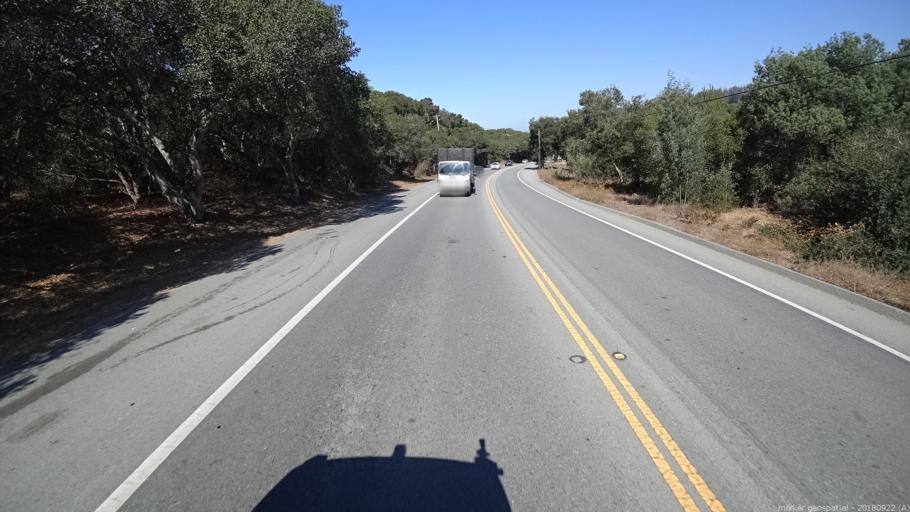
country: US
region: California
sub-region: Monterey County
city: Elkhorn
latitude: 36.8357
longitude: -121.6825
